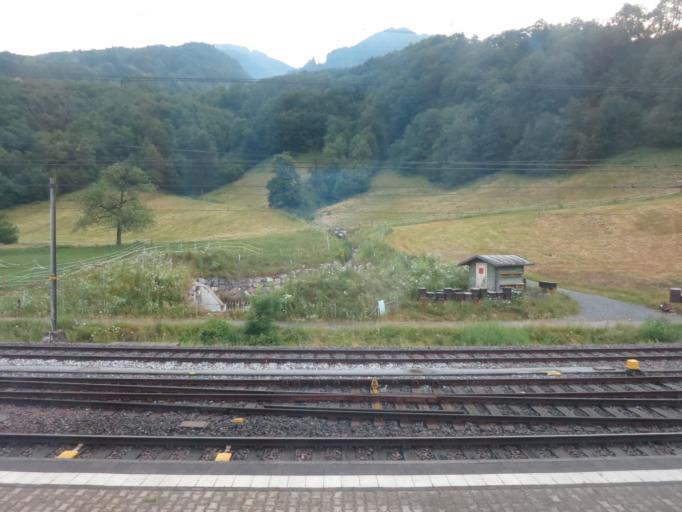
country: CH
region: Glarus
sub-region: Glarus
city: Niederurnen
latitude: 47.1363
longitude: 9.0609
